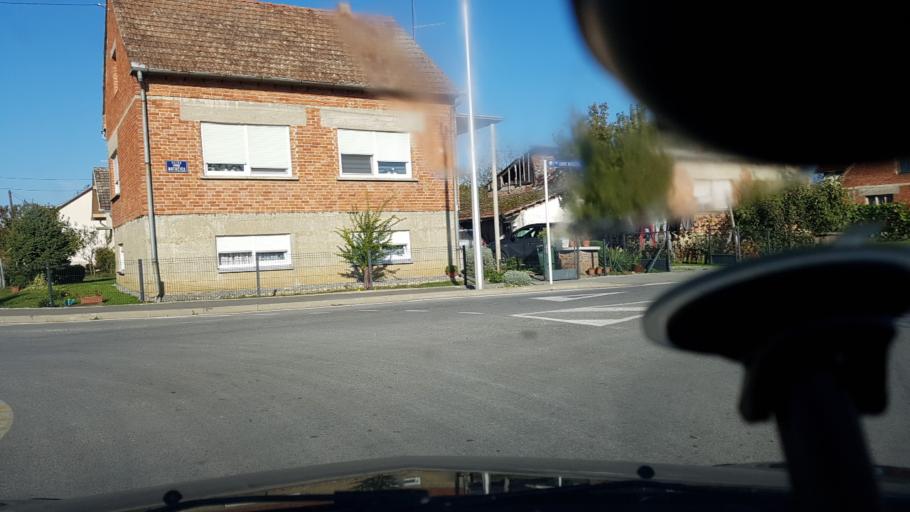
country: HR
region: Bjelovarsko-Bilogorska
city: Bjelovar
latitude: 45.9210
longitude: 16.8621
